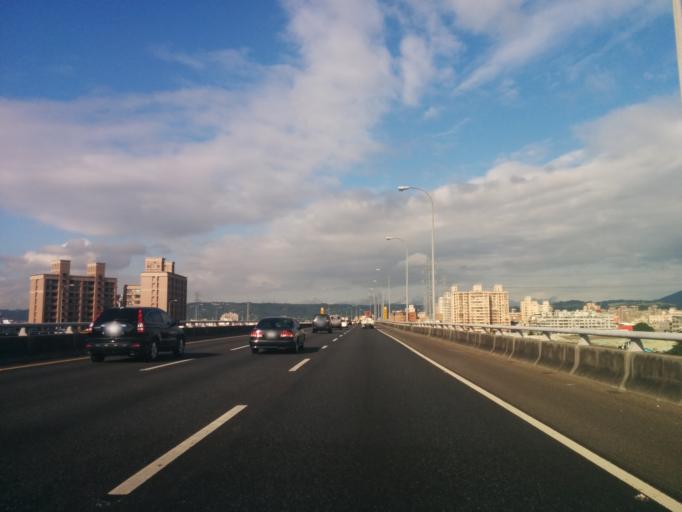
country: TW
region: Taipei
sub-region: Taipei
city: Banqiao
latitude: 25.0750
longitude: 121.4739
